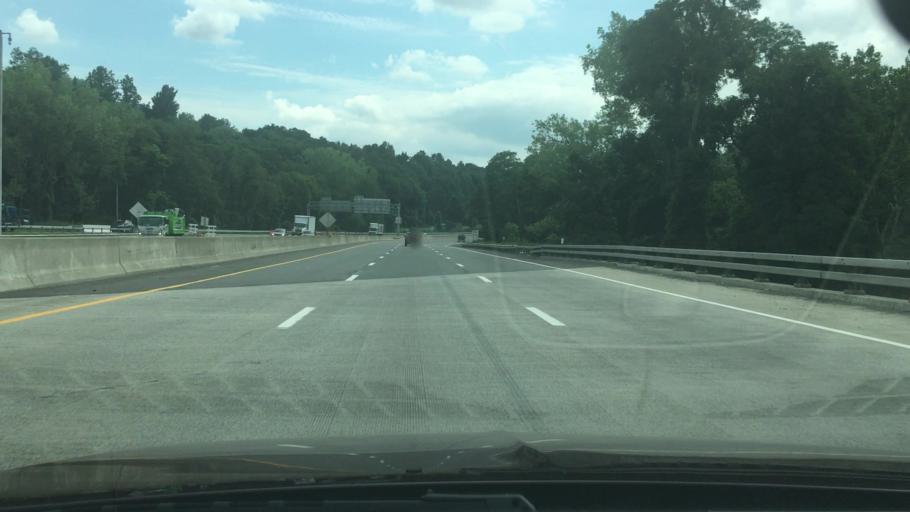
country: US
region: New York
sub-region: Westchester County
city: Greenburgh
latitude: 41.0417
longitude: -73.8363
